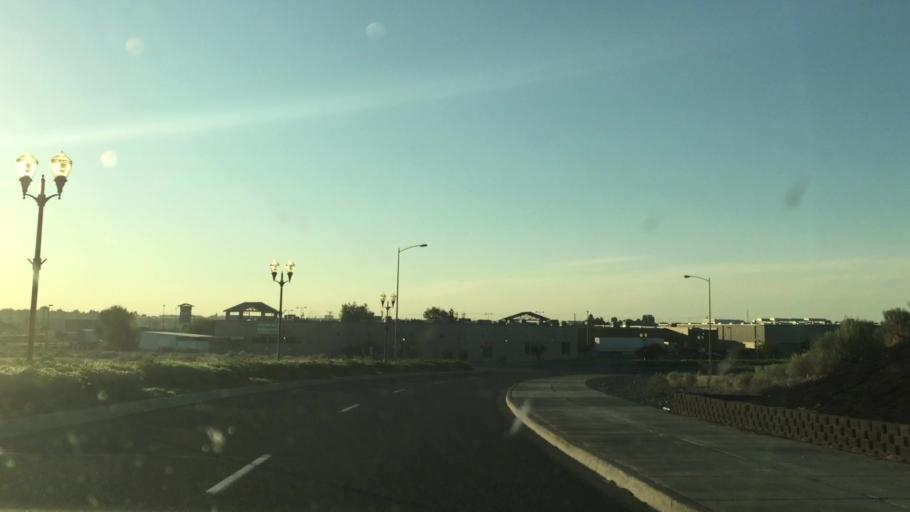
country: US
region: Washington
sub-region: Grant County
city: Moses Lake
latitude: 47.1431
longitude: -119.2854
